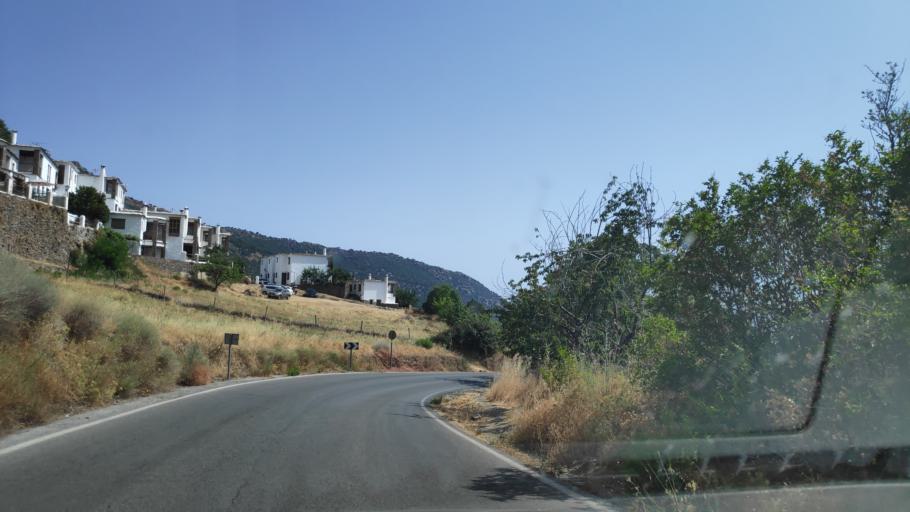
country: ES
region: Andalusia
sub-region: Provincia de Granada
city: Bubion
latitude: 36.9527
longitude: -3.3550
